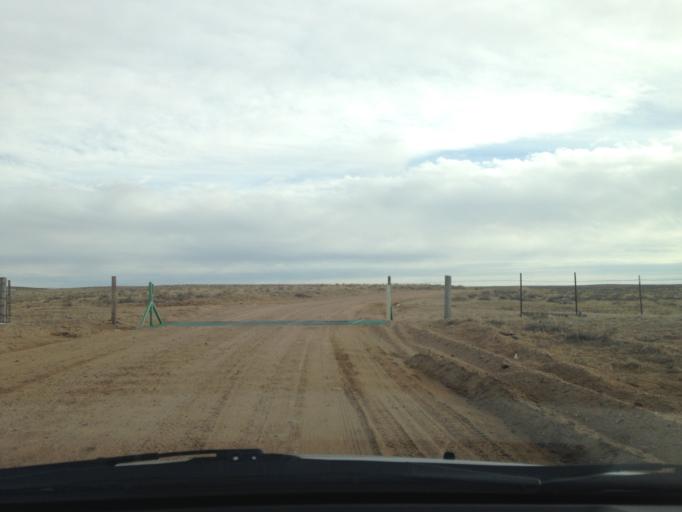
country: US
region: Colorado
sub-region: Weld County
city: Keenesburg
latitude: 40.2326
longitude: -104.2063
